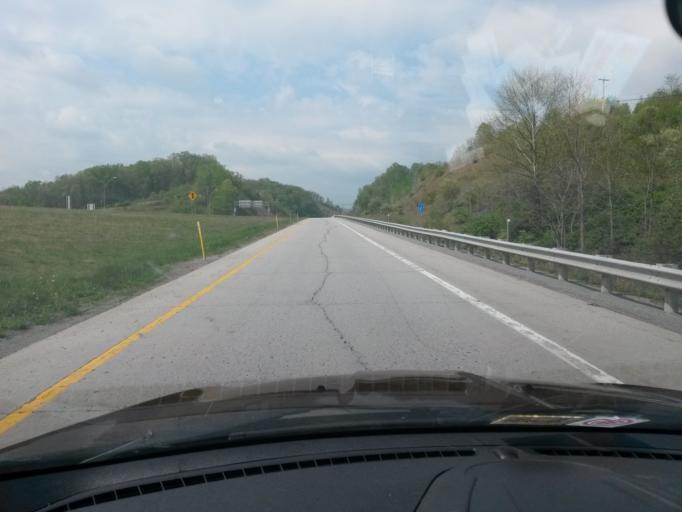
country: US
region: West Virginia
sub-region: Randolph County
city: Elkins
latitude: 38.9541
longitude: -79.8593
